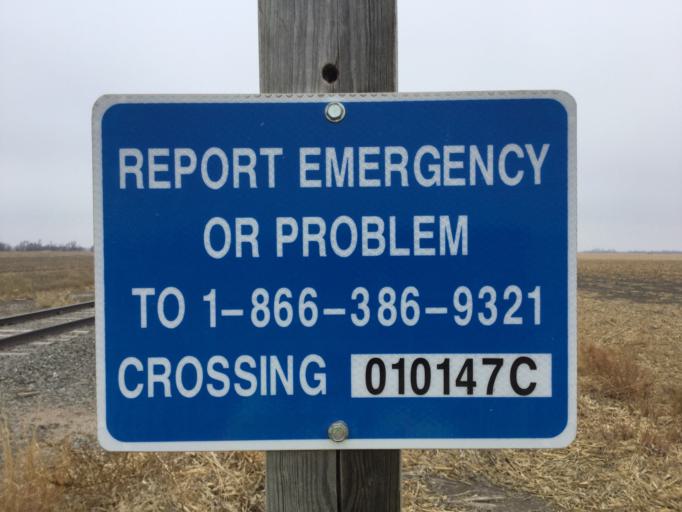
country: US
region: Kansas
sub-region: Edwards County
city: Kinsley
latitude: 38.1969
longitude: -99.4426
